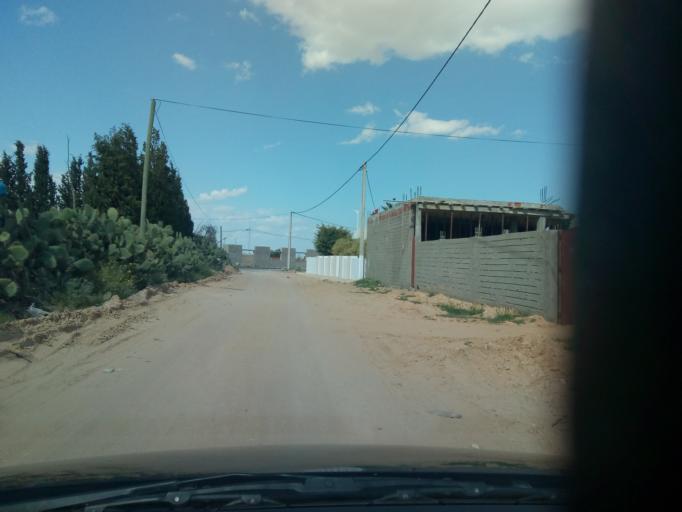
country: TN
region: Safaqis
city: Sfax
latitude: 34.7278
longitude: 10.6108
